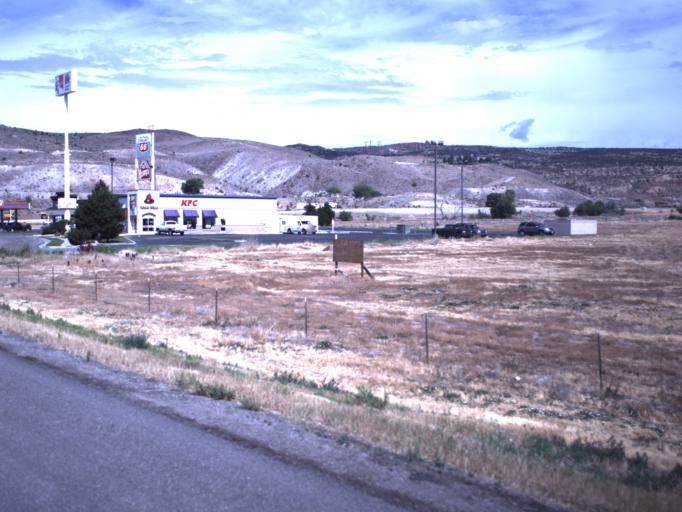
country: US
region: Utah
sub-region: Sevier County
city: Richfield
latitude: 38.7500
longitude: -112.1002
